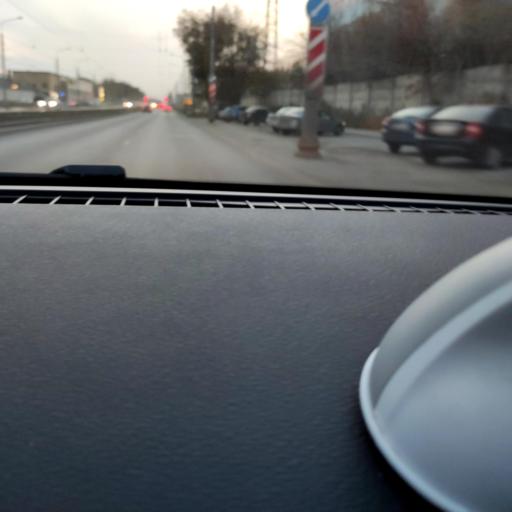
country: RU
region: Samara
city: Samara
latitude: 53.2052
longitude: 50.2713
